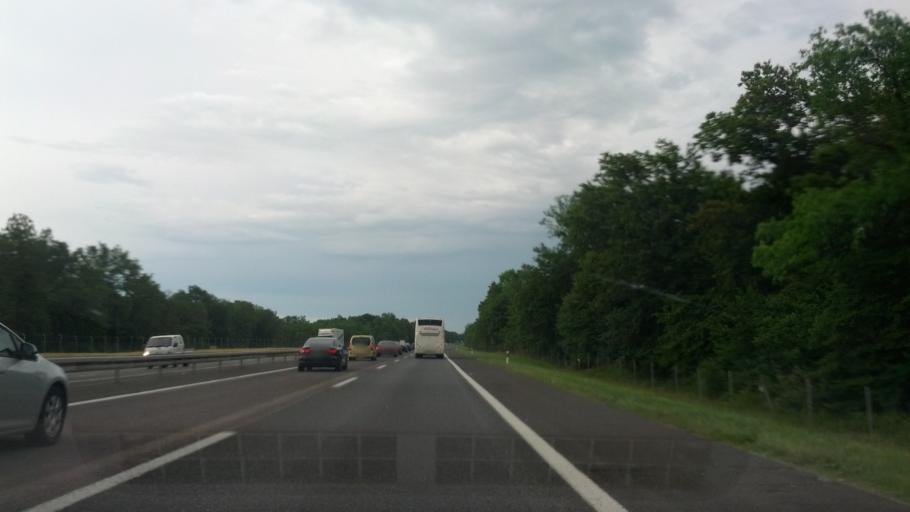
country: HR
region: Zagrebacka
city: Jastrebarsko
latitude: 45.6665
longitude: 15.7214
